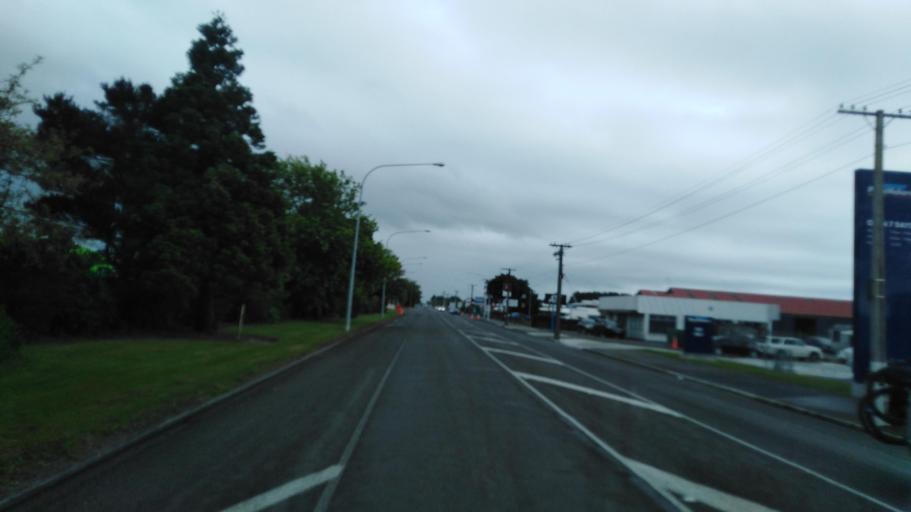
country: NZ
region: Manawatu-Wanganui
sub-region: Horowhenua District
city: Levin
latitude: -40.6350
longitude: 175.2739
